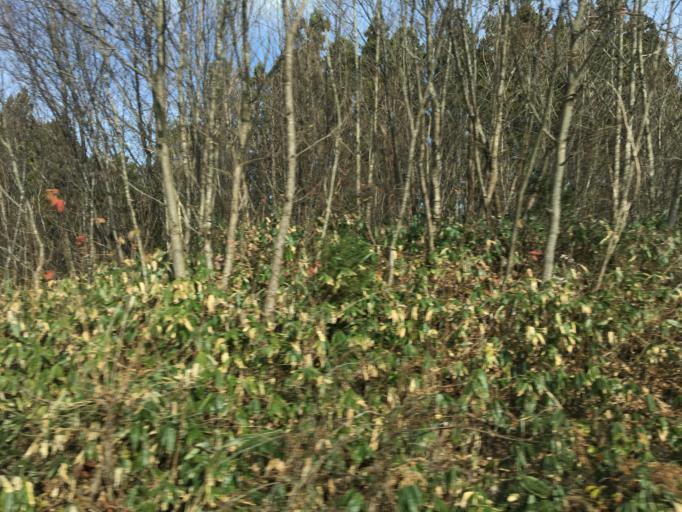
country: JP
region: Akita
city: Omagari
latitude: 39.5443
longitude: 140.3781
